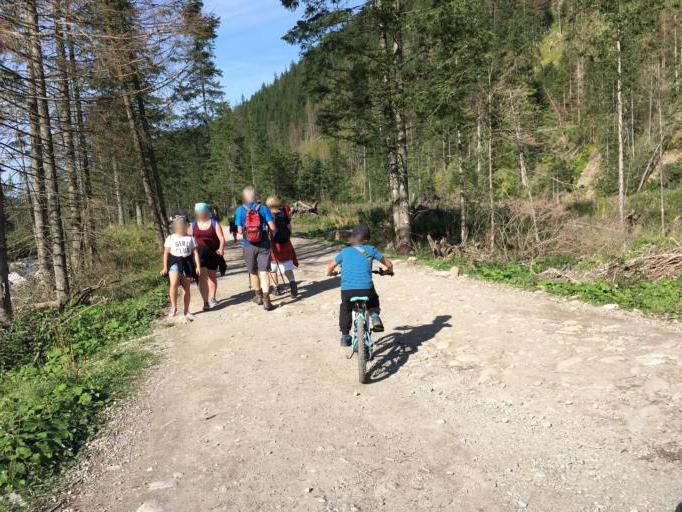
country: PL
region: Lesser Poland Voivodeship
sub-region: Powiat tatrzanski
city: Koscielisko
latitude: 49.2487
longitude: 19.8142
